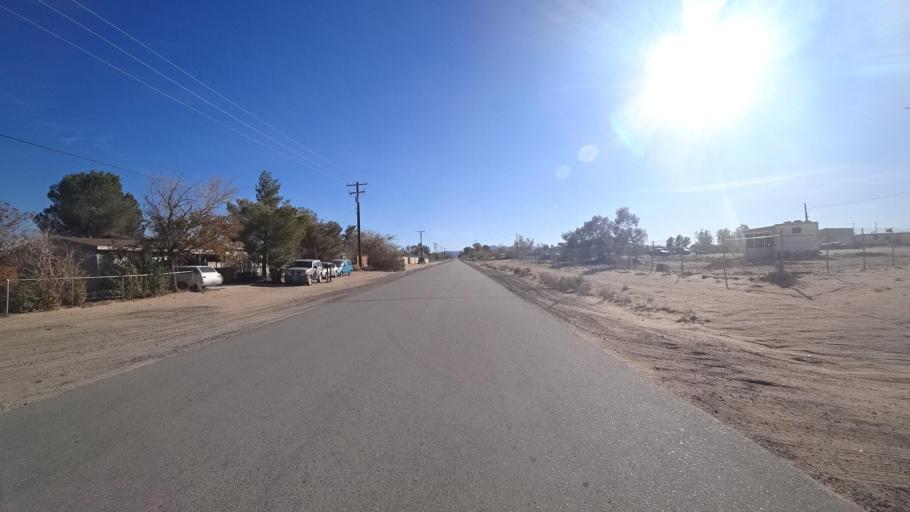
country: US
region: California
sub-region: Kern County
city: China Lake Acres
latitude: 35.6507
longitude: -117.7676
